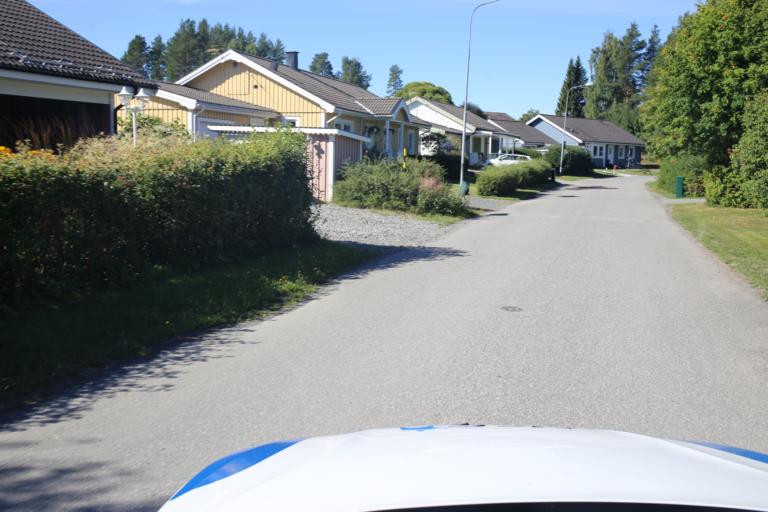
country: SE
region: Vaesterbotten
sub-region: Skelleftea Kommun
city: Viken
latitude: 64.7470
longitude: 20.7729
